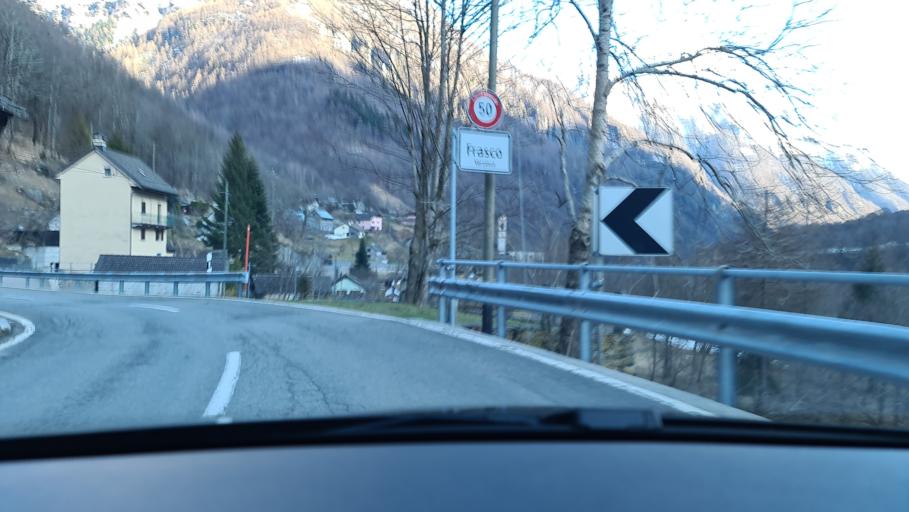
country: CH
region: Ticino
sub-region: Locarno District
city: Lavertezzo
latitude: 46.3427
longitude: 8.7993
